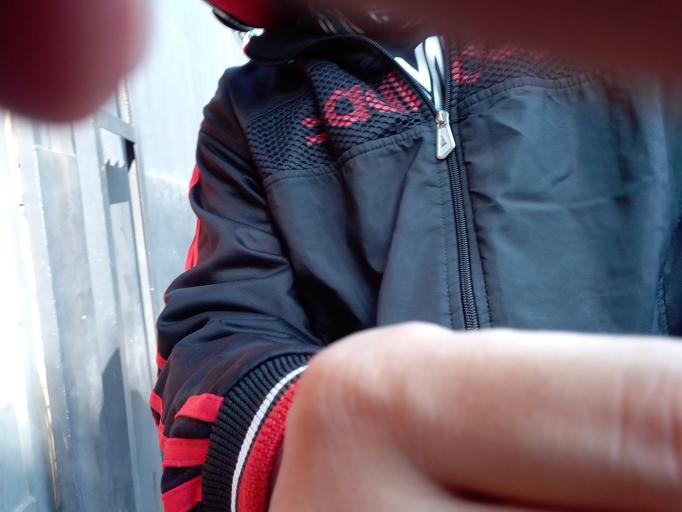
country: ID
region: Jakarta Raya
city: Jakarta
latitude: -6.2659
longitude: 106.8103
